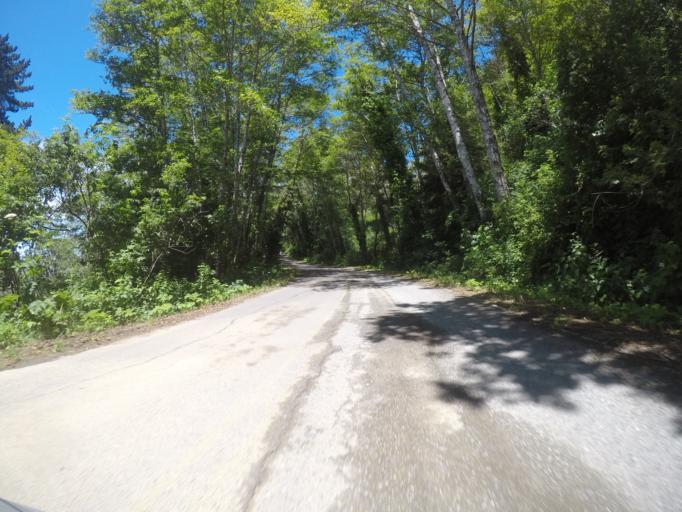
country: US
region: California
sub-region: Del Norte County
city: Bertsch-Oceanview
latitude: 41.5486
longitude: -124.0762
